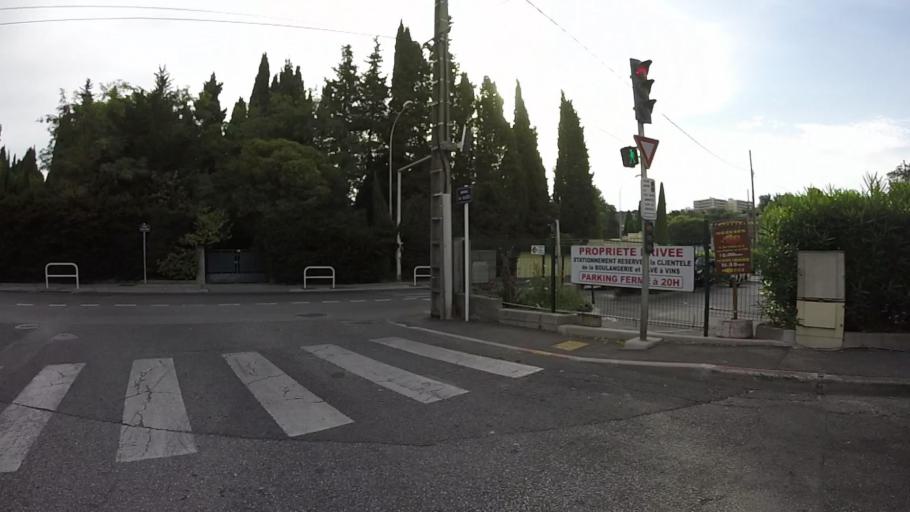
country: FR
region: Provence-Alpes-Cote d'Azur
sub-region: Departement des Alpes-Maritimes
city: Antibes
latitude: 43.5906
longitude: 7.1062
